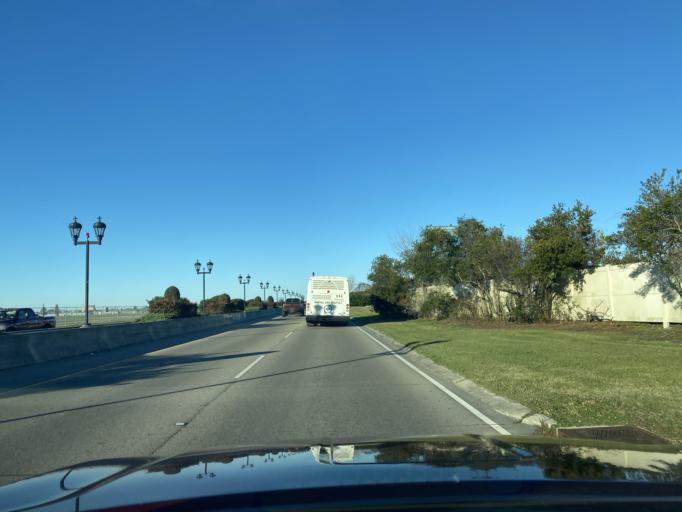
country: US
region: Louisiana
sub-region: Jefferson Parish
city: Kenner
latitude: 29.9964
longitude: -90.2460
